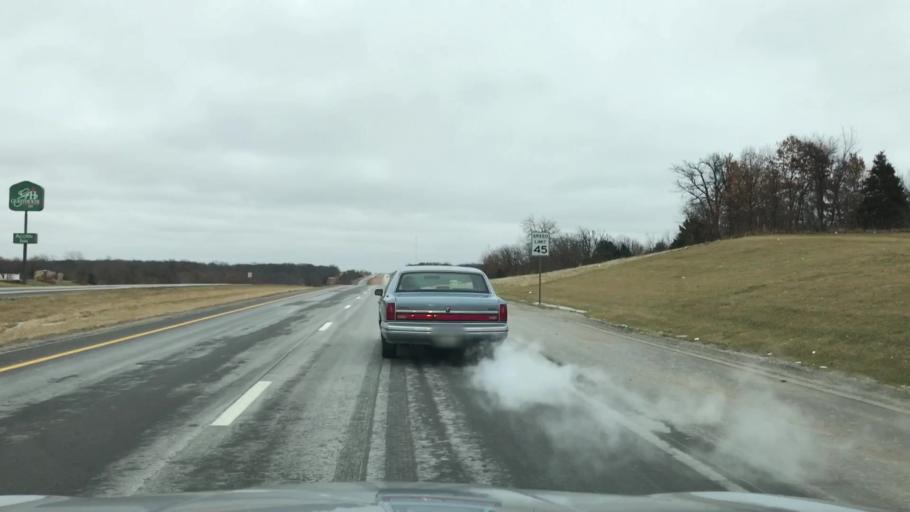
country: US
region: Missouri
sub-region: Clinton County
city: Cameron
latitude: 39.7534
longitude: -94.2149
